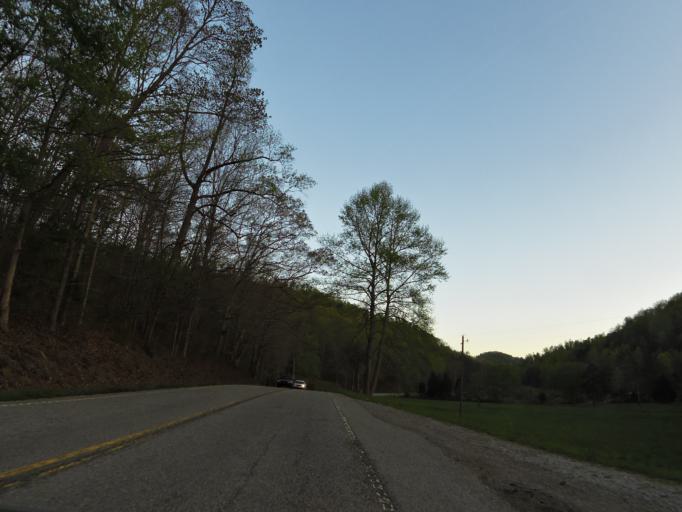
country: US
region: Tennessee
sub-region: Campbell County
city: Fincastle
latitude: 36.4714
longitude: -84.0795
